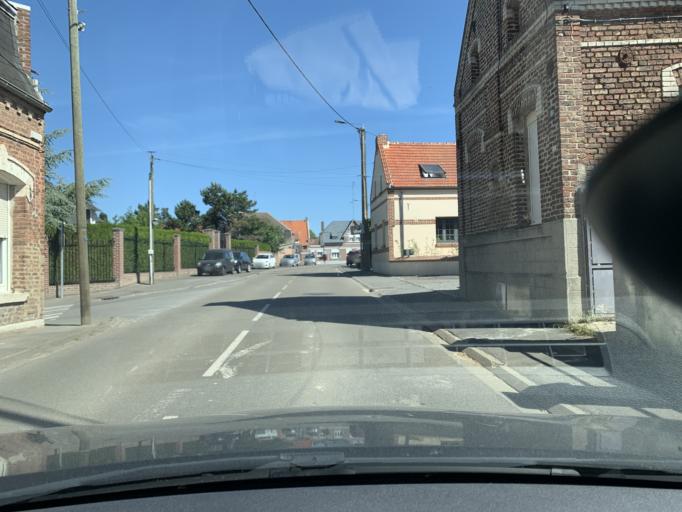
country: FR
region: Nord-Pas-de-Calais
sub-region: Departement du Nord
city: Fontaine-Notre-Dame
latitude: 50.1650
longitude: 3.1563
